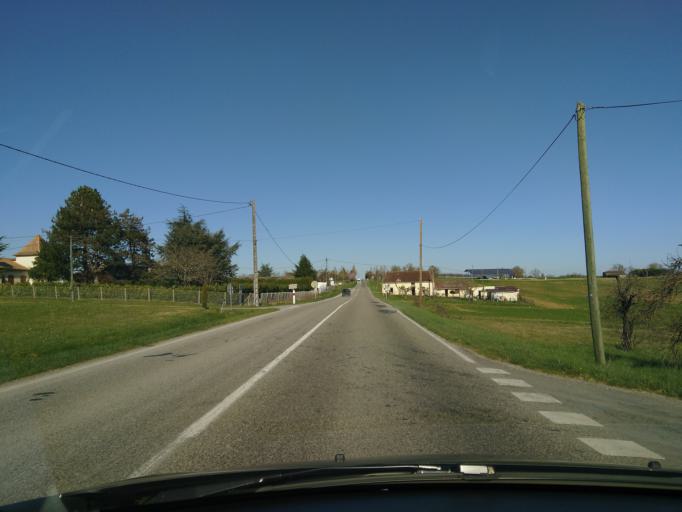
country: FR
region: Aquitaine
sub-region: Departement du Lot-et-Garonne
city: Cancon
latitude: 44.5479
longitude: 0.6258
